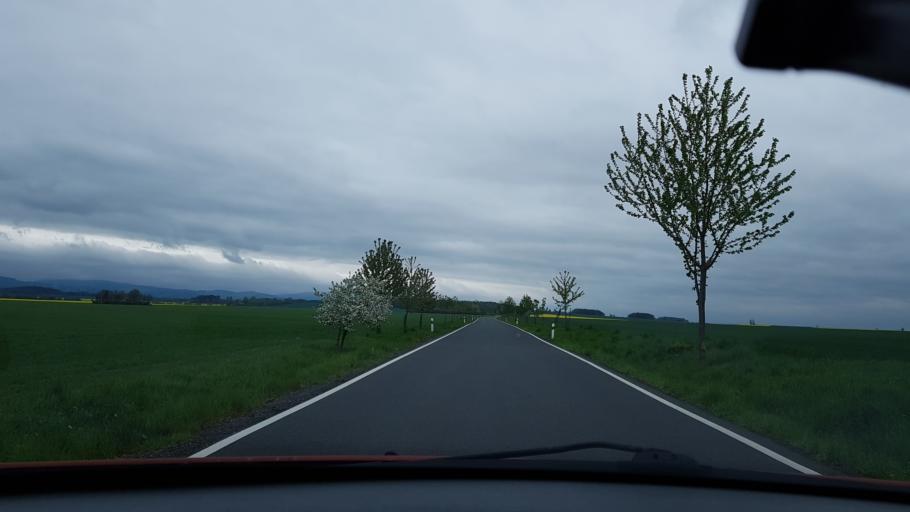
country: CZ
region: Olomoucky
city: Vidnava
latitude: 50.3778
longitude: 17.1693
